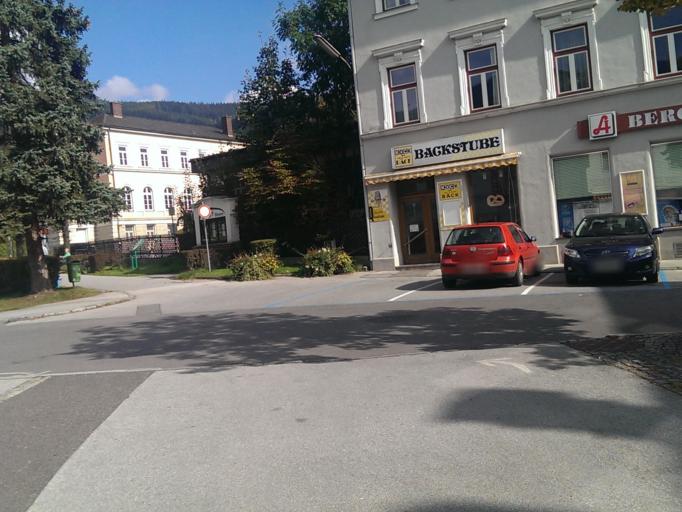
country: AT
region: Styria
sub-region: Politischer Bezirk Bruck-Muerzzuschlag
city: Muerzzuschlag
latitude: 47.6071
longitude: 15.6751
